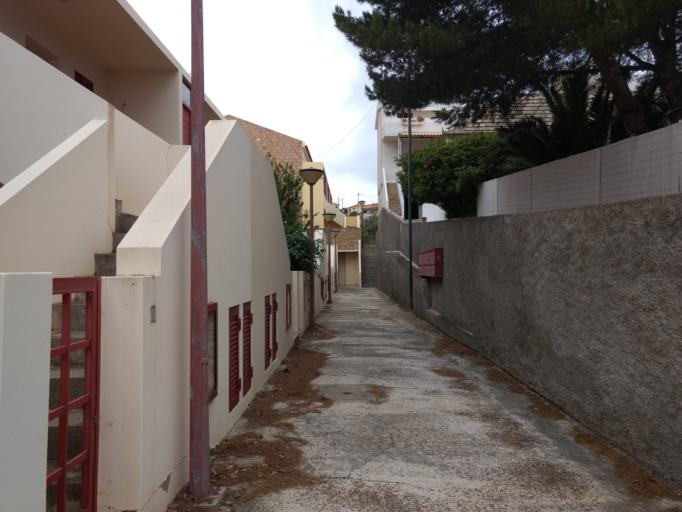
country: PT
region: Madeira
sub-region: Porto Santo
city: Vila de Porto Santo
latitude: 33.0607
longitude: -16.3309
